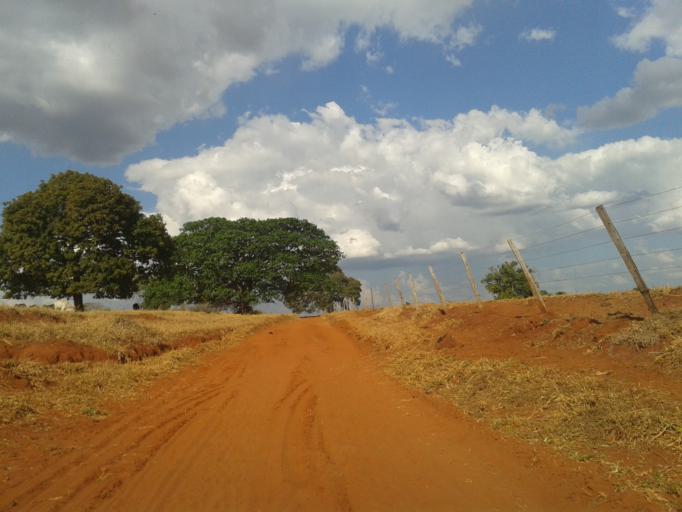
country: BR
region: Minas Gerais
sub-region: Santa Vitoria
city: Santa Vitoria
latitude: -19.1632
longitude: -50.0125
